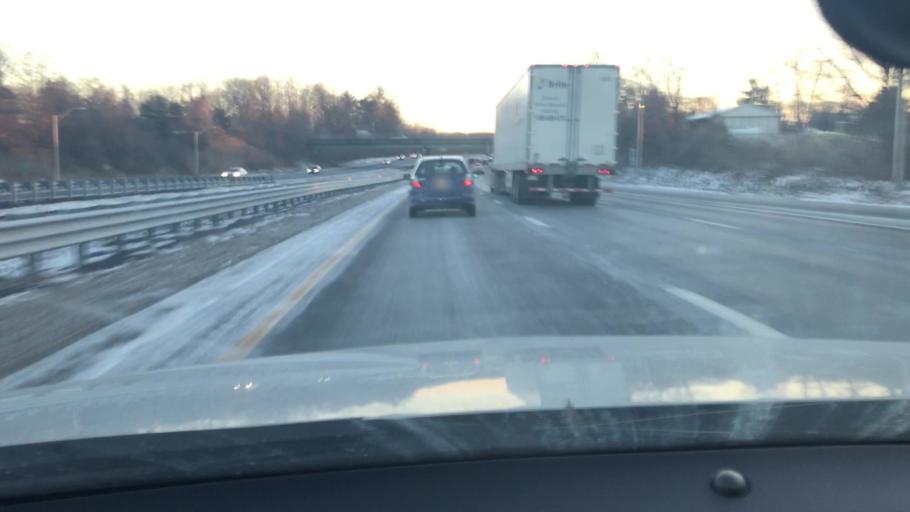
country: US
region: New Jersey
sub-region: Burlington County
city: Bordentown
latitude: 40.1329
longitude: -74.7155
